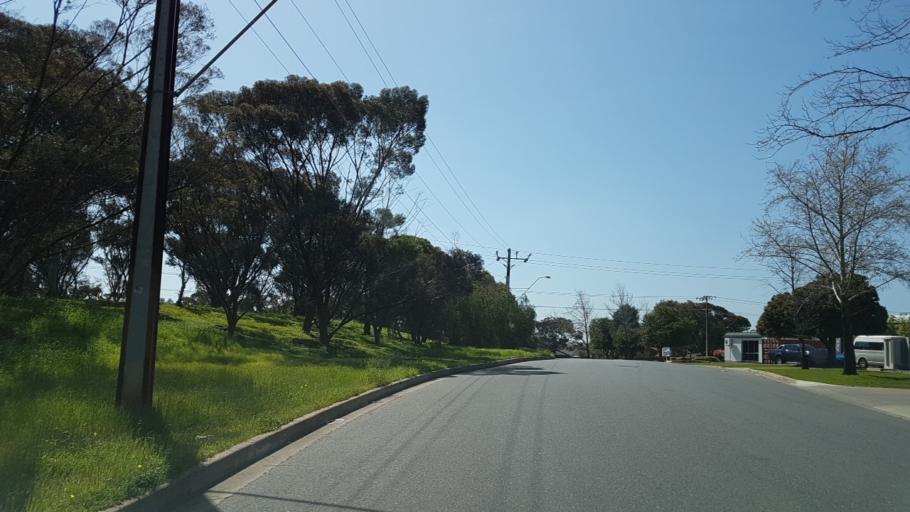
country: AU
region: South Australia
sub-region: Tea Tree Gully
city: Modbury
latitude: -34.8455
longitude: 138.6785
